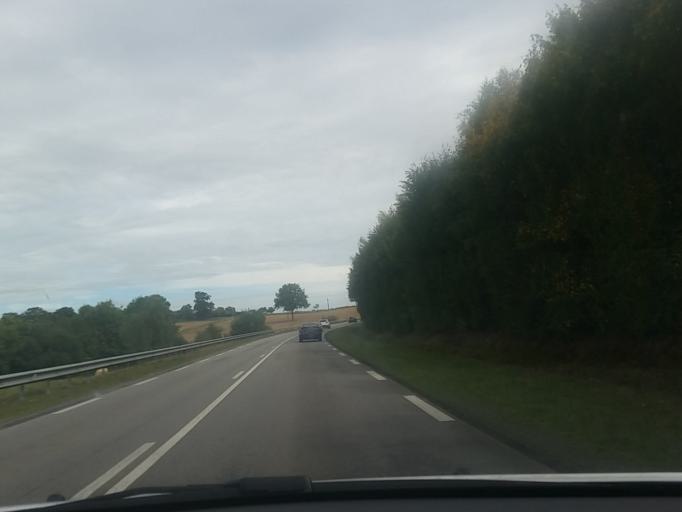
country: FR
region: Brittany
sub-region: Departement d'Ille-et-Vilaine
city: Martigne-Ferchaud
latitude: 47.8123
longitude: -1.3284
